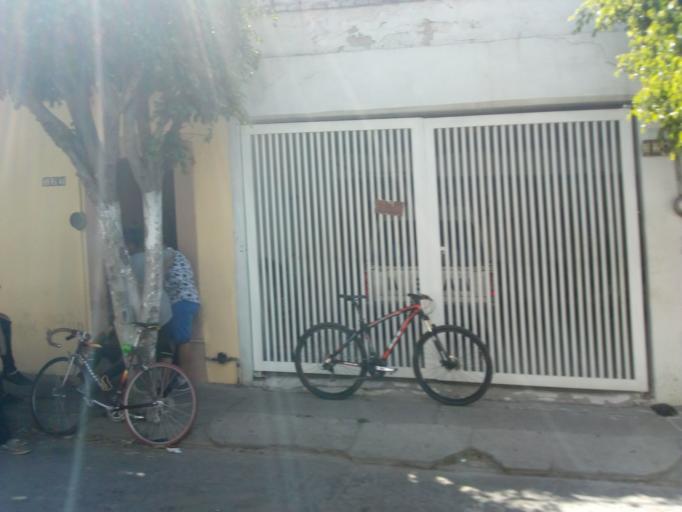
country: MX
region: Guanajuato
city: Leon
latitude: 21.1370
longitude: -101.6853
